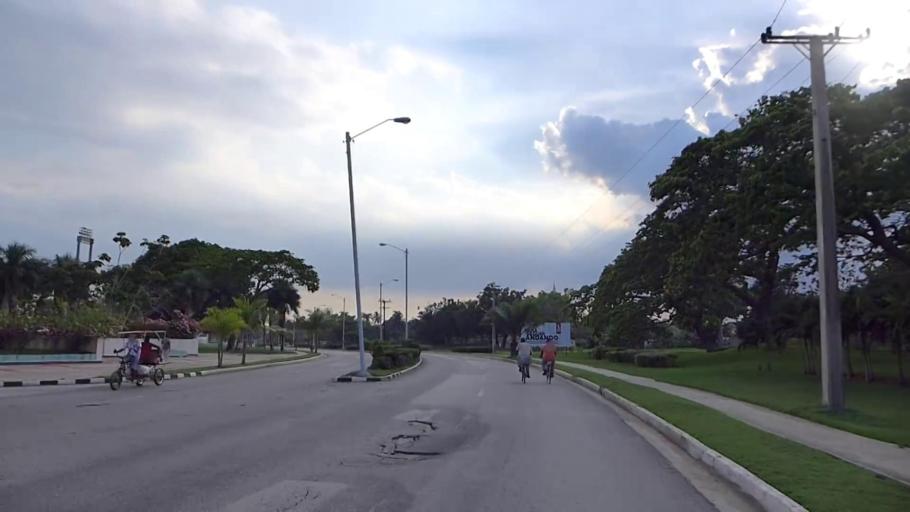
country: CU
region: Camaguey
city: Camaguey
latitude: 21.3809
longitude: -77.9107
